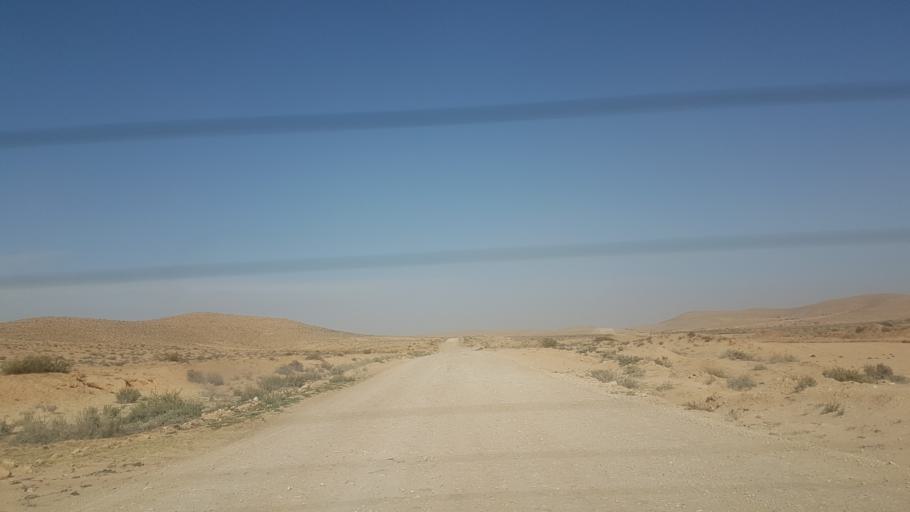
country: TN
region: Qabis
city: Matmata
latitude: 33.6415
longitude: 9.7370
